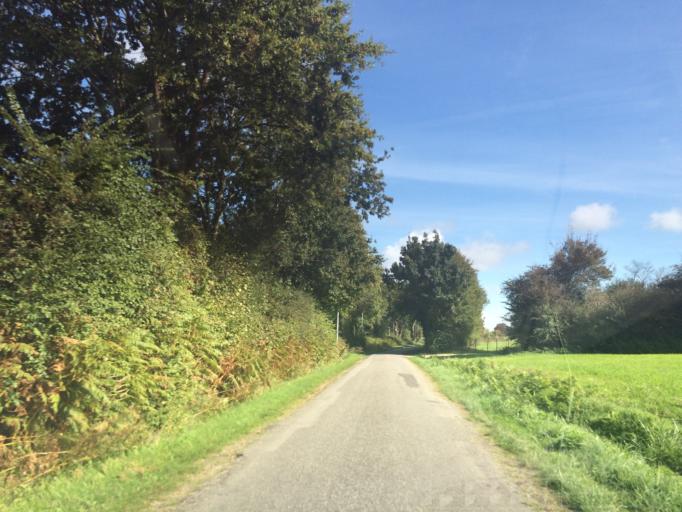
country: FR
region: Pays de la Loire
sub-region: Departement de la Loire-Atlantique
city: Chemere
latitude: 47.1318
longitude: -1.9251
